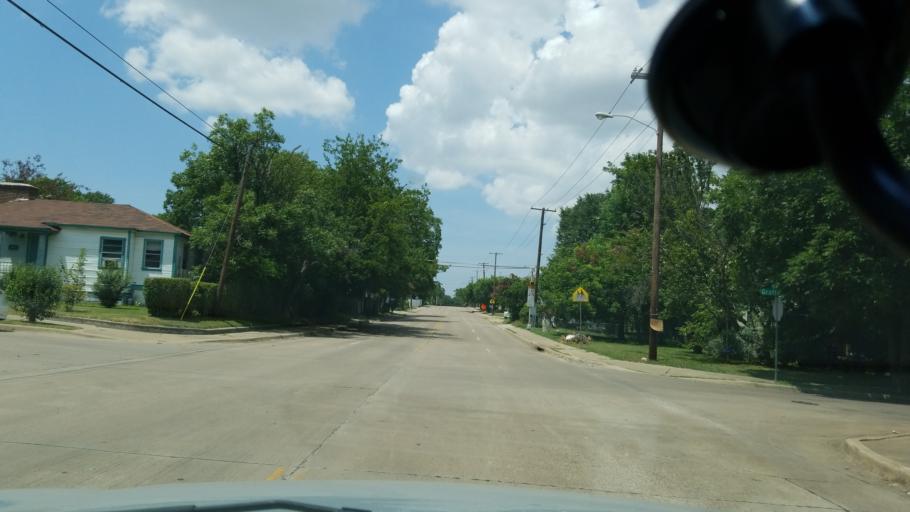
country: US
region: Texas
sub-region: Dallas County
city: Cockrell Hill
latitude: 32.7307
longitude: -96.8689
